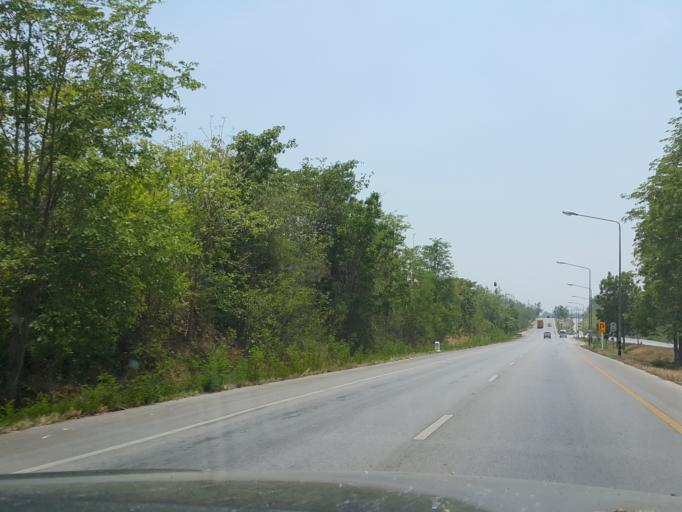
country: TH
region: Lampang
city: Thoen
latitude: 17.6040
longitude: 99.2259
